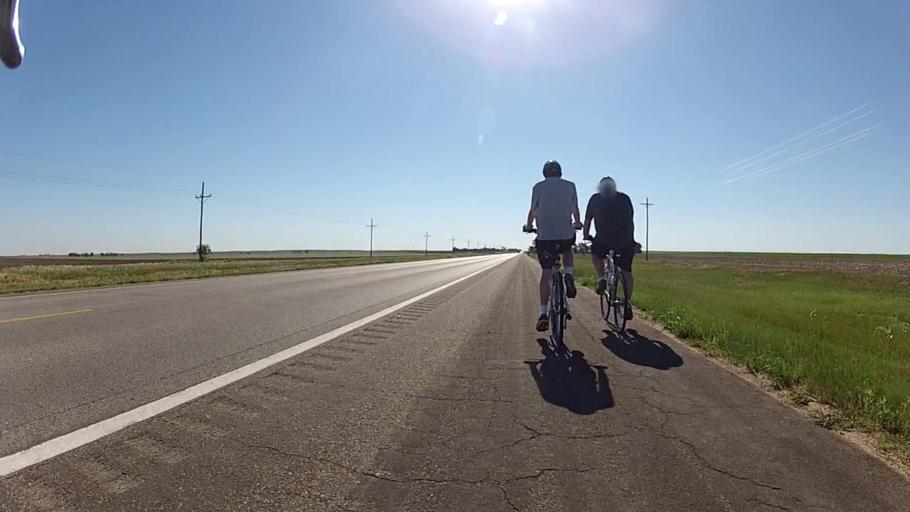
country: US
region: Kansas
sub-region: Kiowa County
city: Greensburg
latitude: 37.5863
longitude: -99.6031
